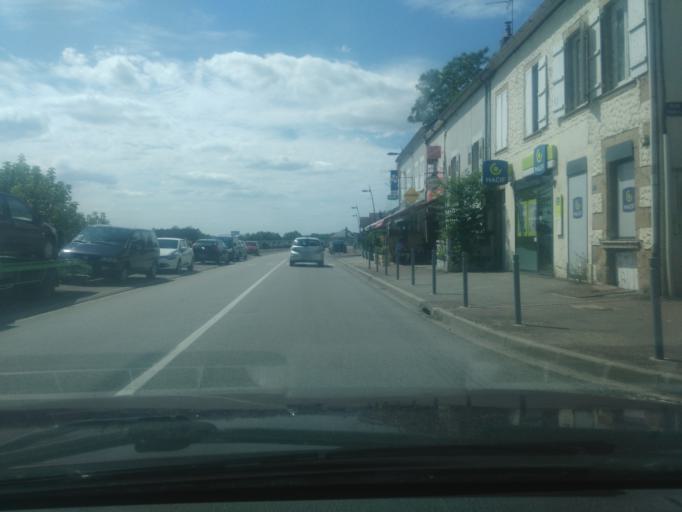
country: FR
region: Bourgogne
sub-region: Departement de la Nievre
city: Saint-Leger-des-Vignes
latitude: 46.8386
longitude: 3.4523
